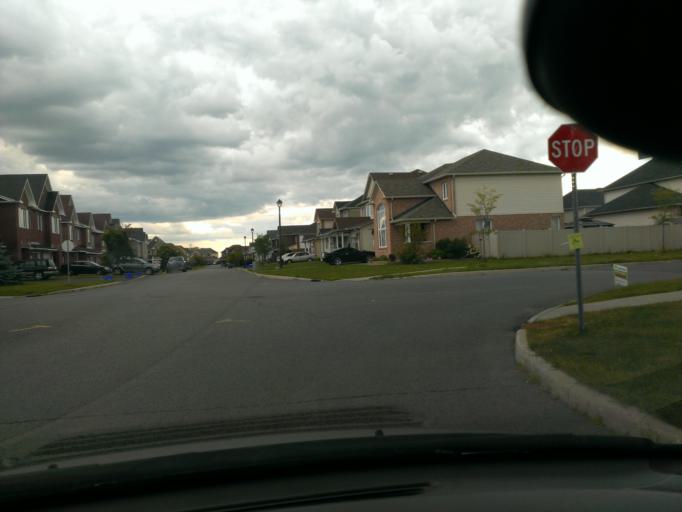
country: CA
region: Ontario
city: Clarence-Rockland
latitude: 45.4506
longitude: -75.4764
